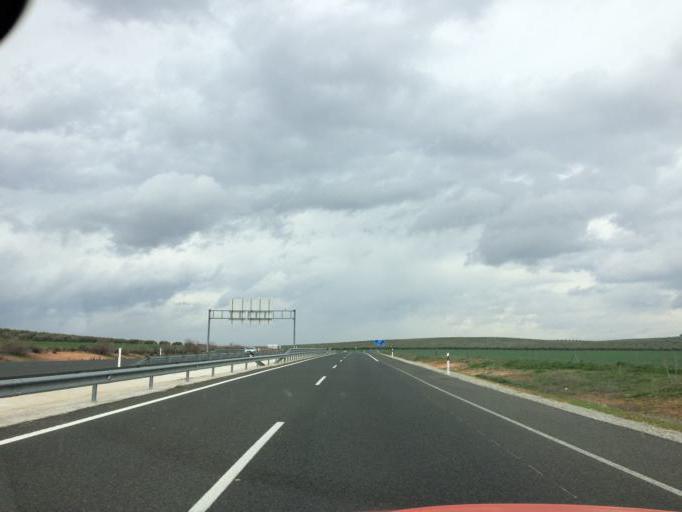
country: ES
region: Andalusia
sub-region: Provincia de Malaga
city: Antequera
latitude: 37.0770
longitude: -4.5328
